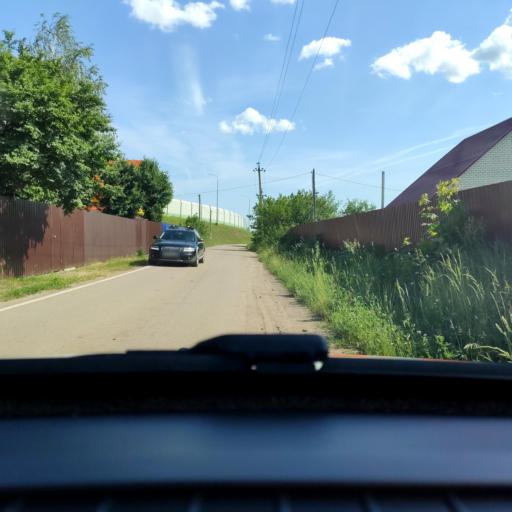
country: RU
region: Voronezj
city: Ramon'
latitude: 51.8228
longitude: 39.2485
